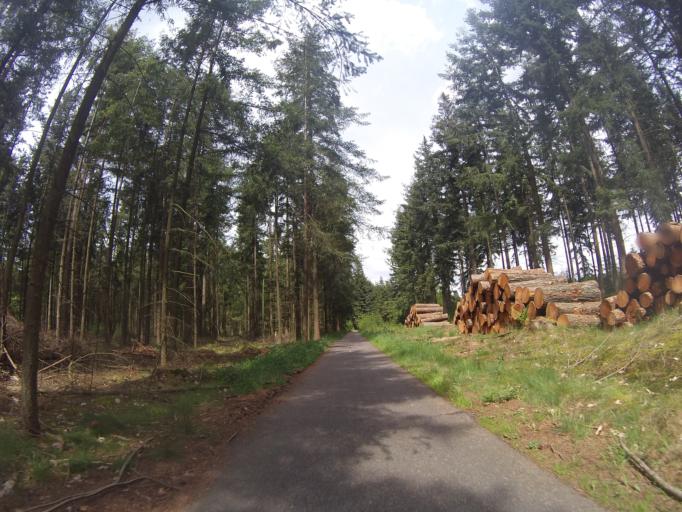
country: NL
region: Drenthe
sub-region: Gemeente Assen
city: Assen
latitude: 52.9035
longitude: 6.6532
